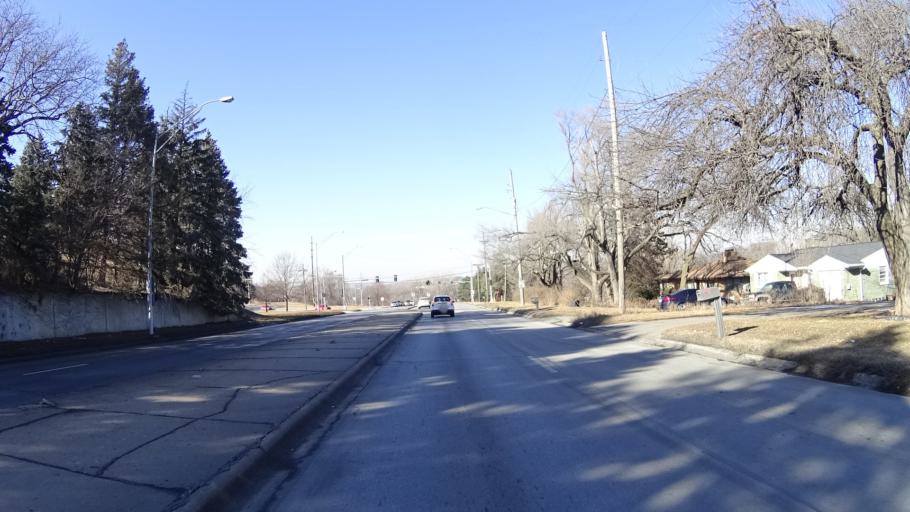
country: US
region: Nebraska
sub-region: Douglas County
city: Ralston
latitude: 41.3058
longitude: -96.0368
